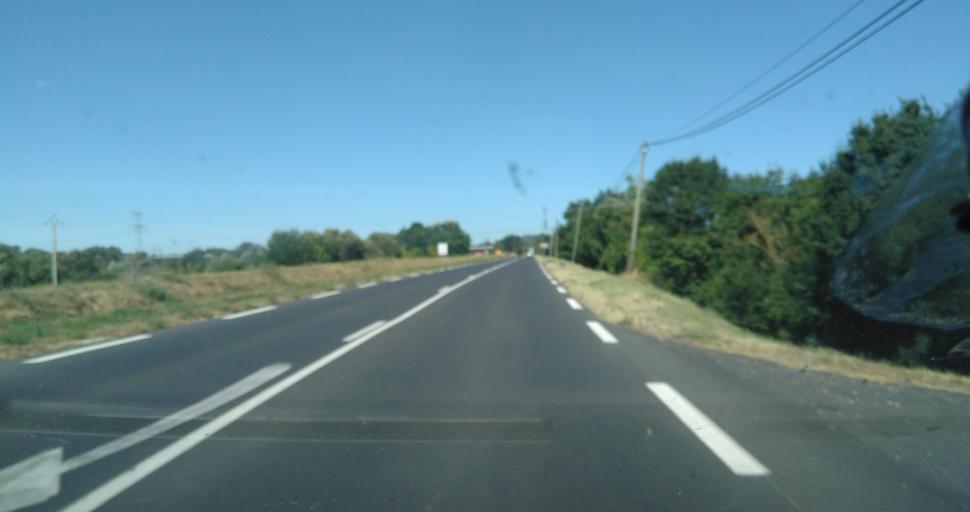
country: FR
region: Centre
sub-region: Departement d'Indre-et-Loire
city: Montlouis-sur-Loire
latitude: 47.3993
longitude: 0.8184
